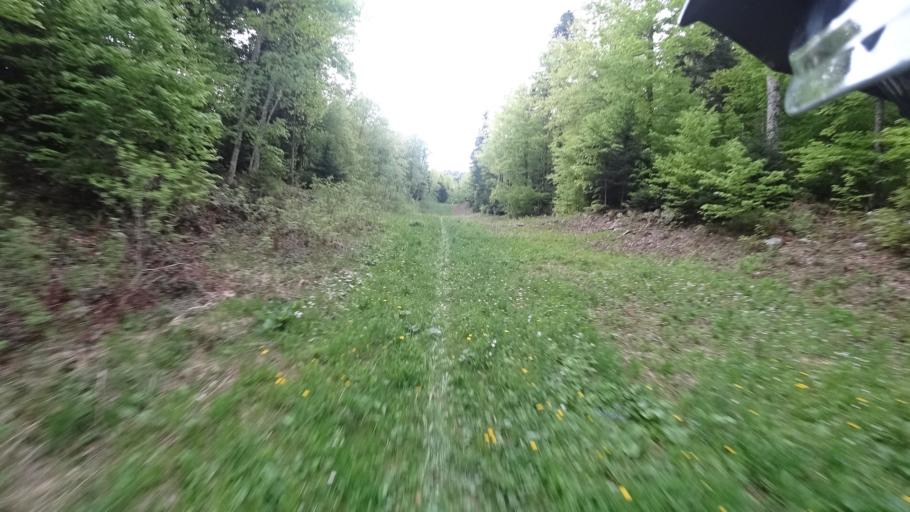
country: HR
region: Karlovacka
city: Plaski
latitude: 44.9267
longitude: 15.4262
